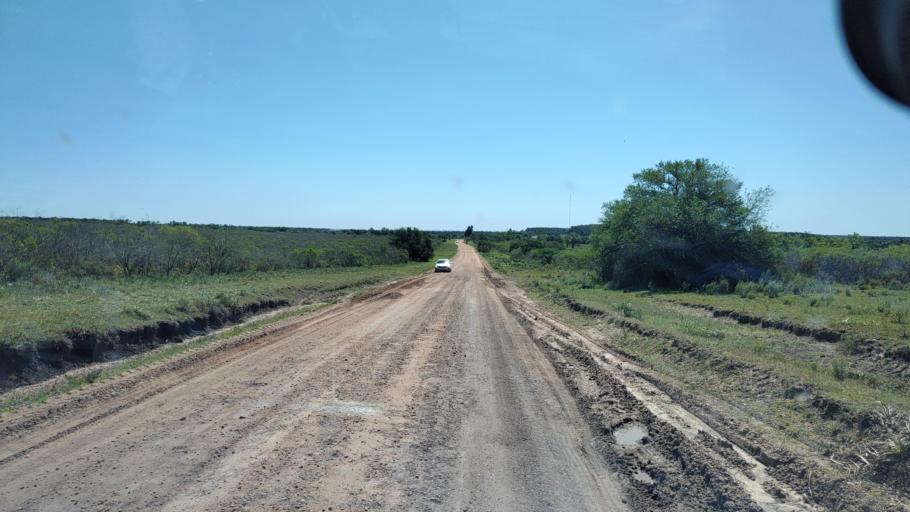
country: AR
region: Entre Rios
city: Ubajay
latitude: -31.8666
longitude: -58.2534
